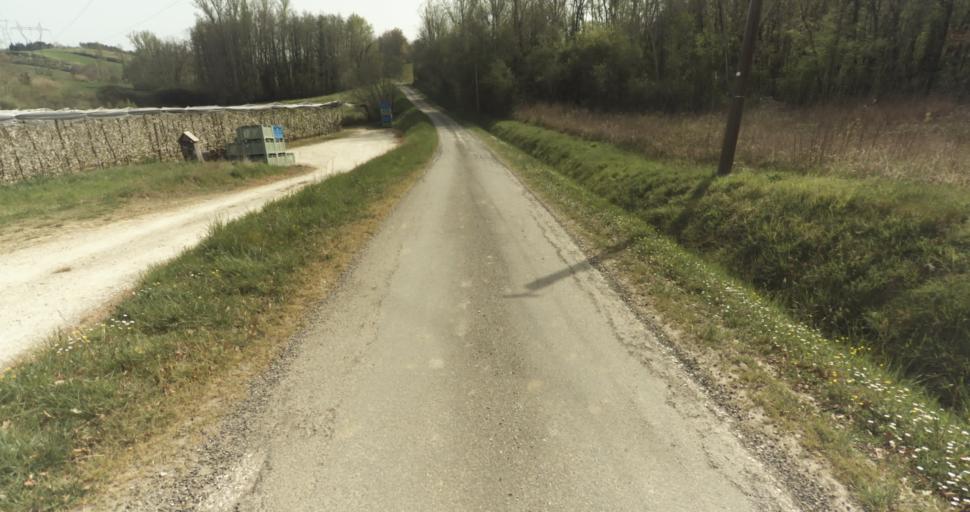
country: FR
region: Midi-Pyrenees
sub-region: Departement du Tarn-et-Garonne
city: Moissac
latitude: 44.1458
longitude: 1.1575
